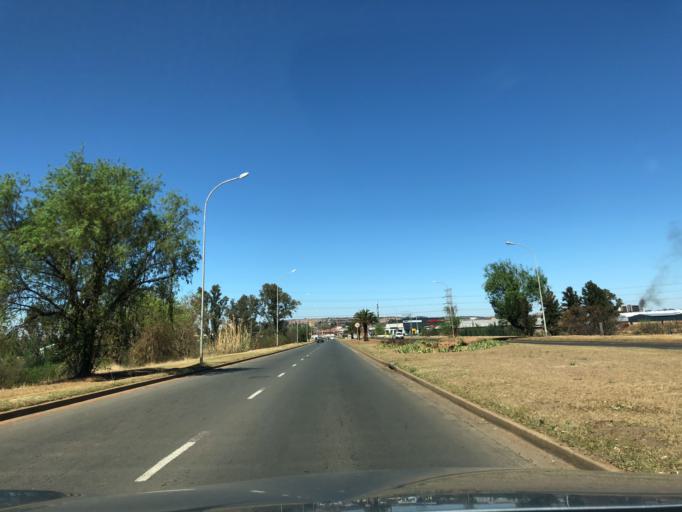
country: ZA
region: KwaZulu-Natal
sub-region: Amajuba District Municipality
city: Newcastle
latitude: -27.7452
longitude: 29.9375
